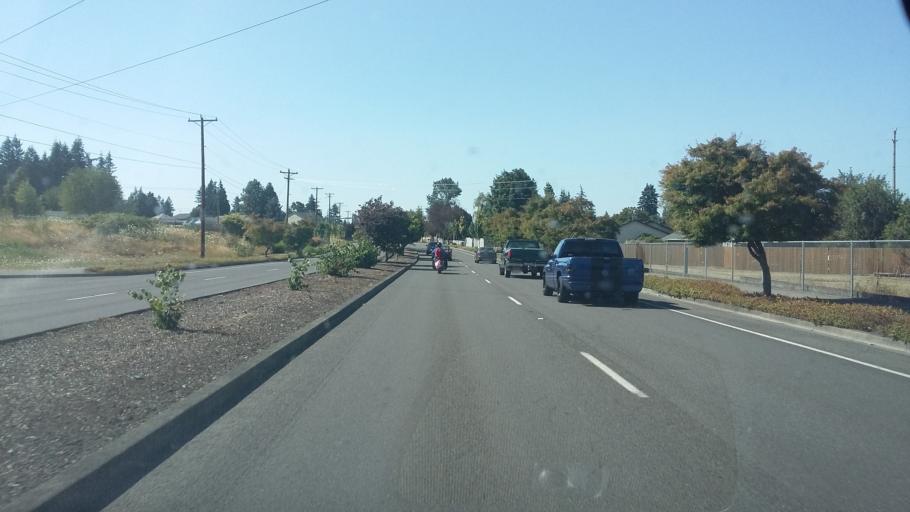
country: US
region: Washington
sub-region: Clark County
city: Orchards
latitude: 45.6699
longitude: -122.5655
